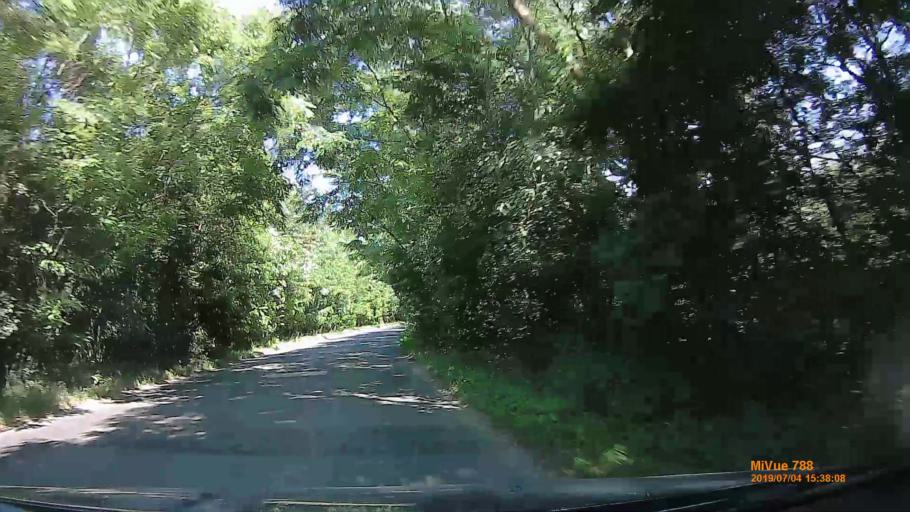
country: HU
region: Komarom-Esztergom
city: Tatabanya
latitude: 47.5552
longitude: 18.3916
